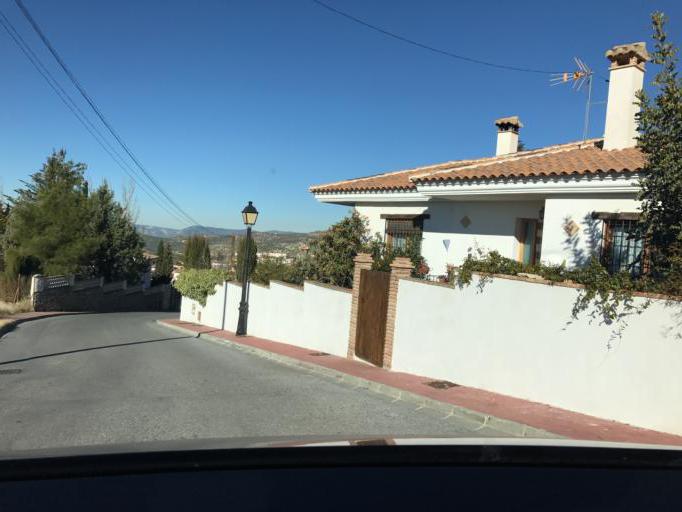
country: ES
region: Andalusia
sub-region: Provincia de Granada
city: Viznar
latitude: 37.2344
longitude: -3.5605
